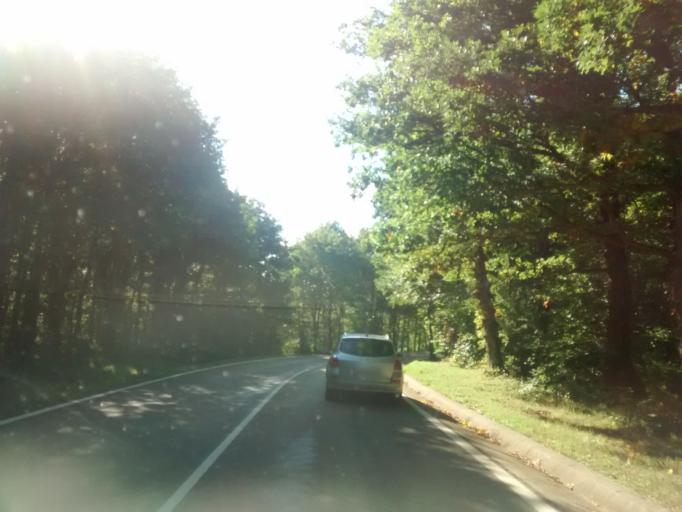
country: ES
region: Cantabria
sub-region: Provincia de Cantabria
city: Reinosa
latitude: 42.9557
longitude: -4.0552
